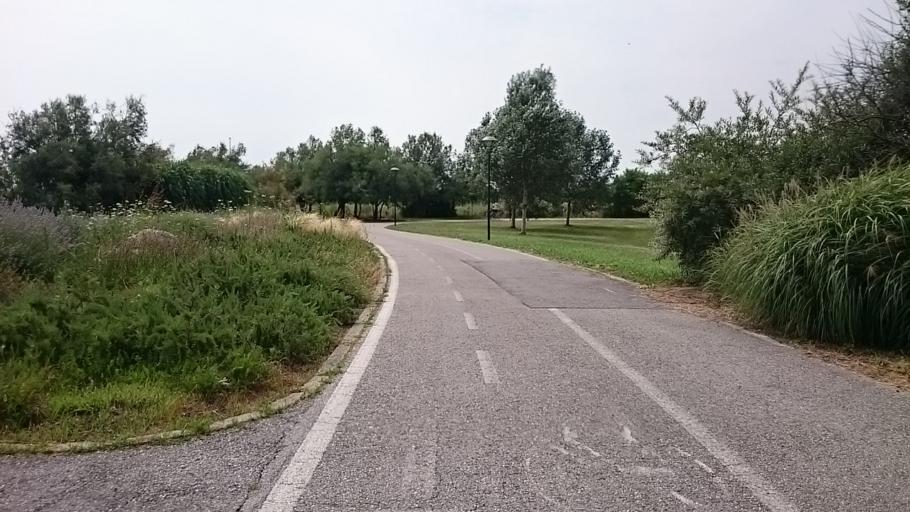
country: IT
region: Veneto
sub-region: Provincia di Venezia
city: Campalto
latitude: 45.4719
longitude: 12.2818
